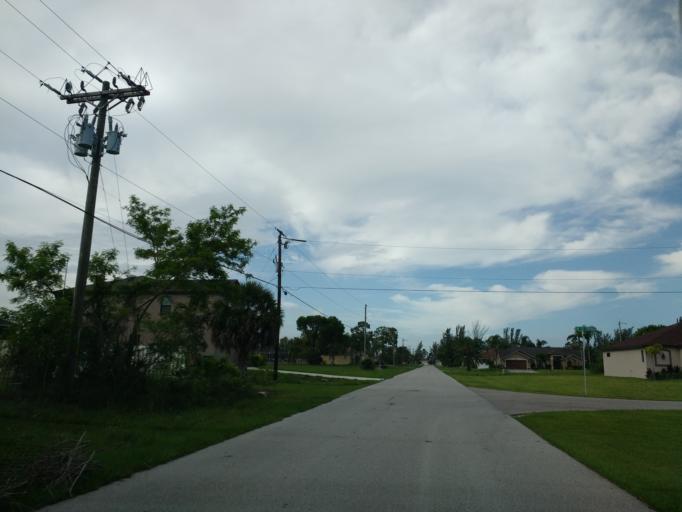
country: US
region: Florida
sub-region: Lee County
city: Cape Coral
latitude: 26.6148
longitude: -82.0198
